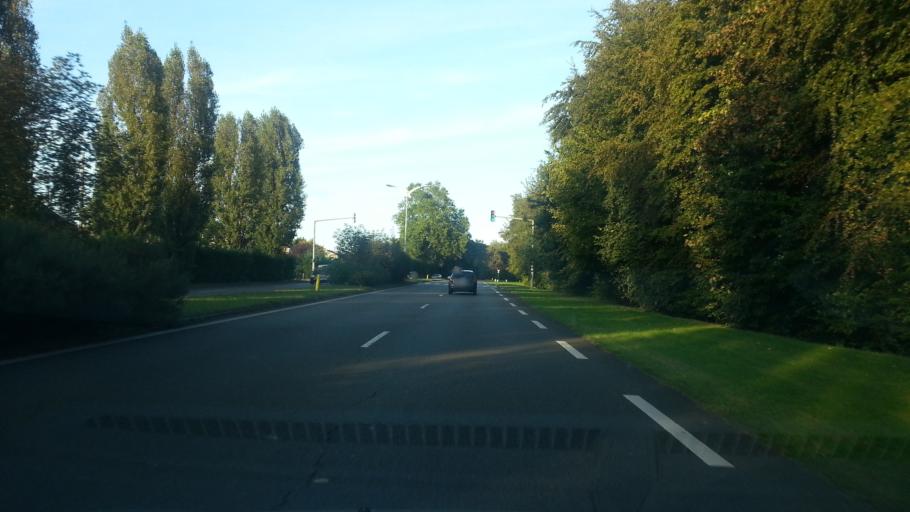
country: FR
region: Picardie
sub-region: Departement de l'Oise
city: Venette
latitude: 49.3986
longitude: 2.8121
